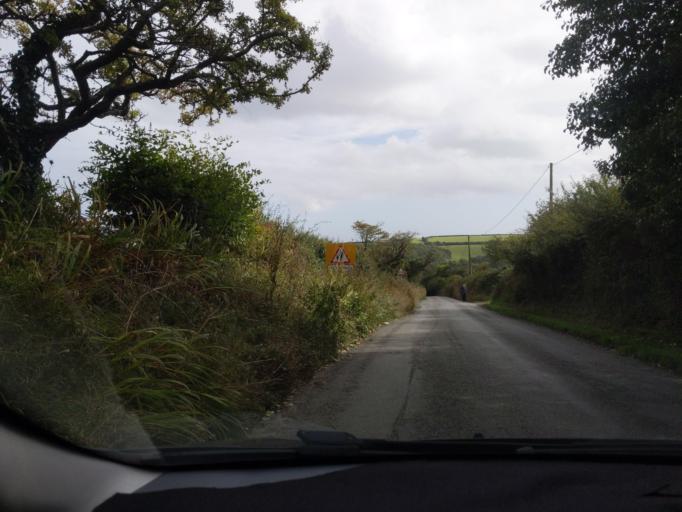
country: GB
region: England
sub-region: Cornwall
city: Mevagissey
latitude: 50.2440
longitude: -4.8004
